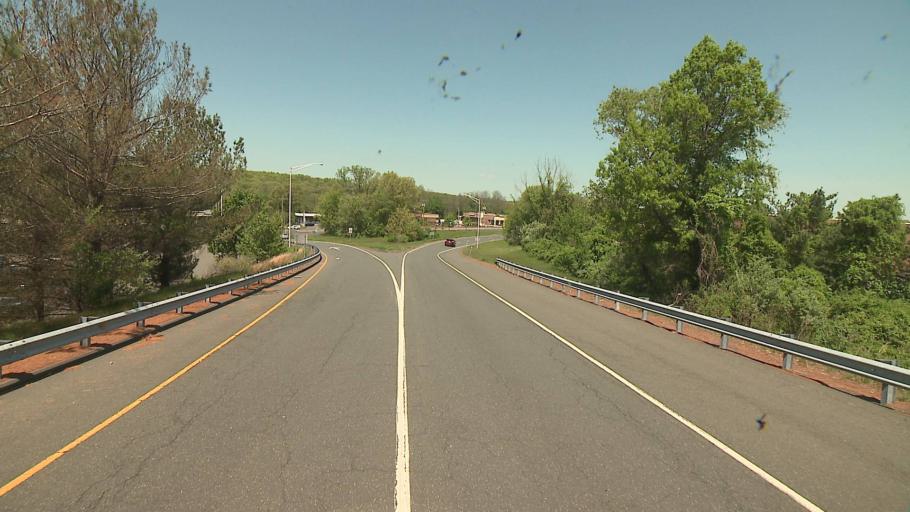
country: US
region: Connecticut
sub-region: Hartford County
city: Manchester
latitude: 41.8270
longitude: -72.4948
